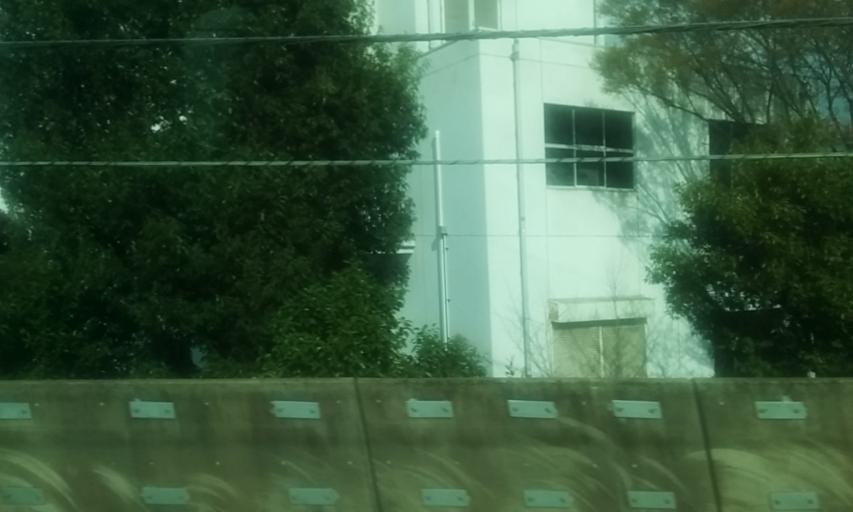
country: JP
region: Kanagawa
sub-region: Kawasaki-shi
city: Kawasaki
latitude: 35.5170
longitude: 139.6798
